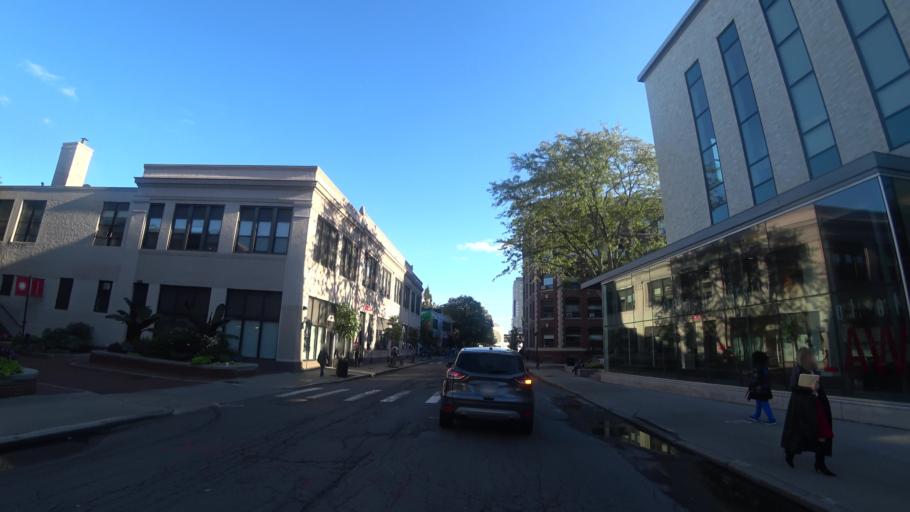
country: US
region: Massachusetts
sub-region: Norfolk County
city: Brookline
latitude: 42.3388
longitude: -71.0902
